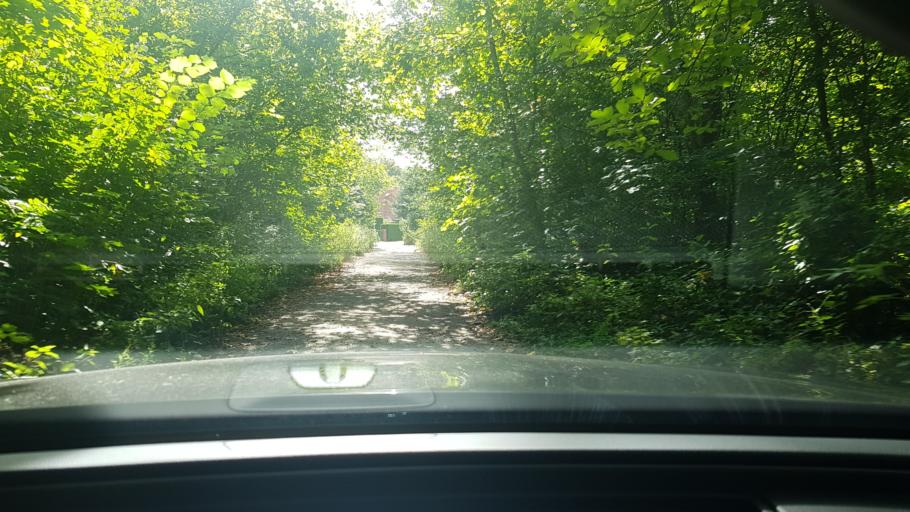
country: DE
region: Brandenburg
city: Brieselang
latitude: 52.5954
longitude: 13.0059
